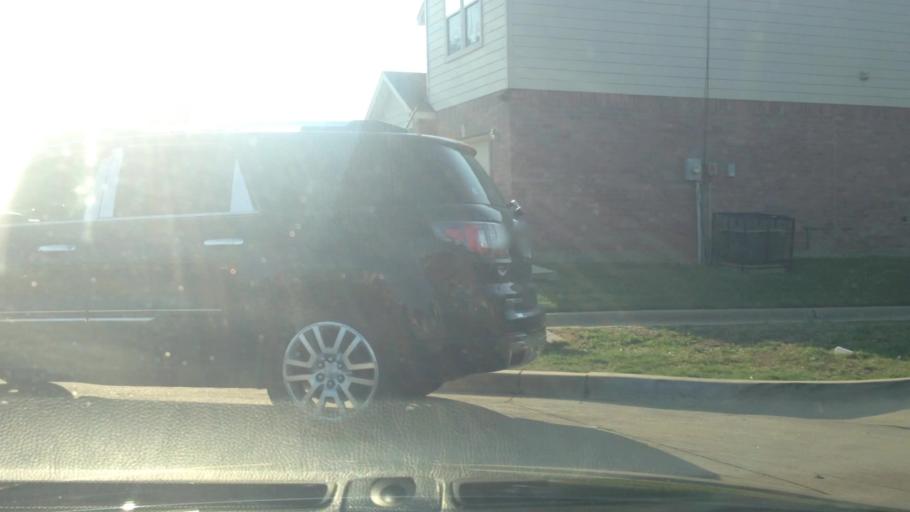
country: US
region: Texas
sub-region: Tarrant County
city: Everman
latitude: 32.6489
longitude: -97.2786
